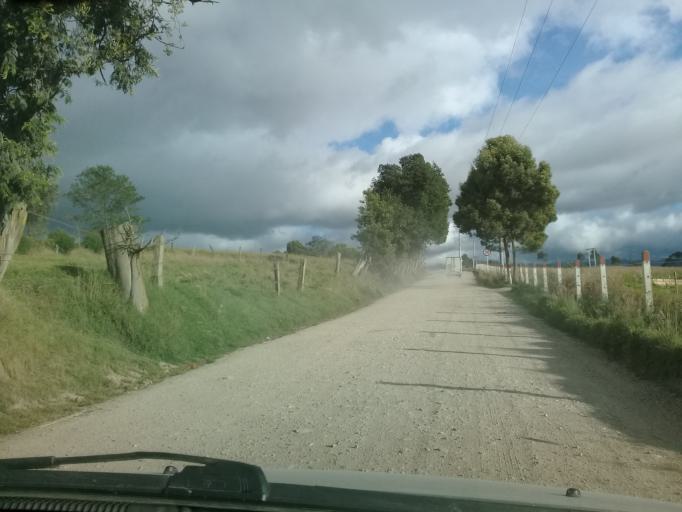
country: CO
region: Cundinamarca
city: Villapinzon
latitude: 5.2396
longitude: -73.6526
